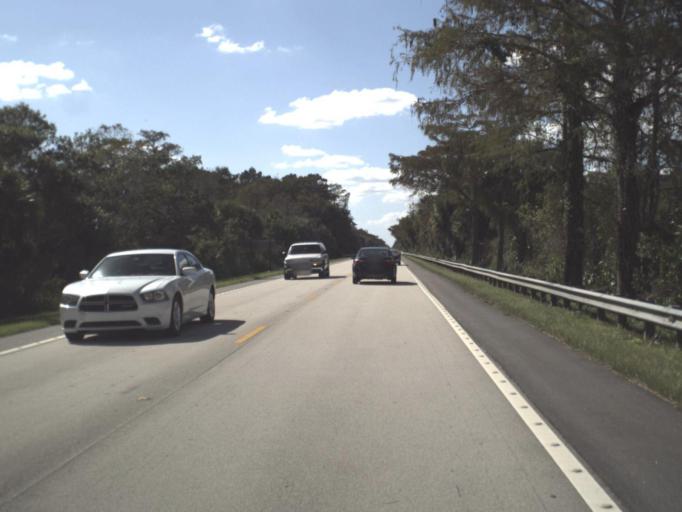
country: US
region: Florida
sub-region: Collier County
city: Marco
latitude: 25.8717
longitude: -81.1788
